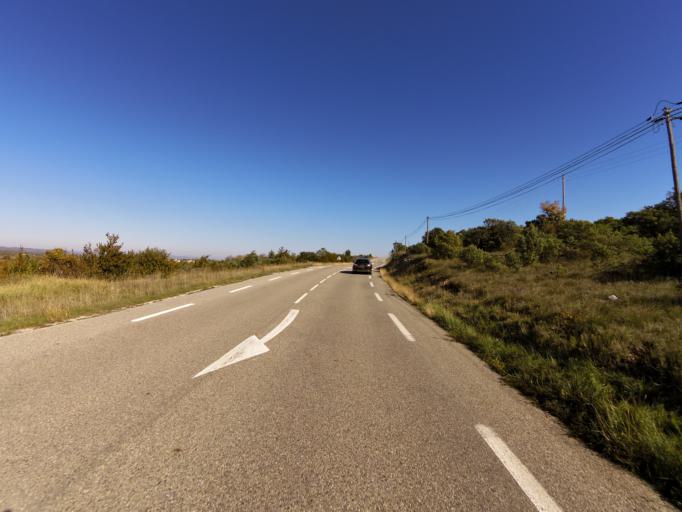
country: FR
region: Languedoc-Roussillon
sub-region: Departement du Gard
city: Saint-Julien-de-Peyrolas
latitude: 44.3850
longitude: 4.5257
